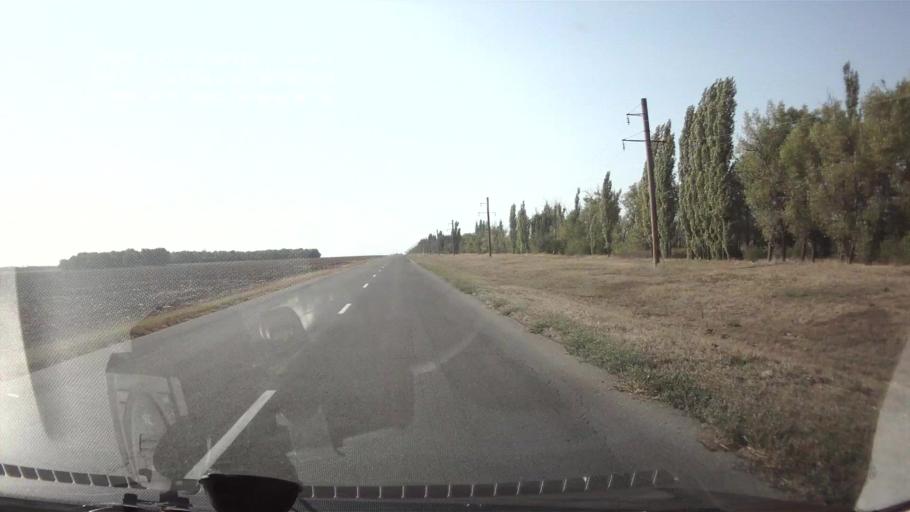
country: RU
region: Rostov
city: Tselina
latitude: 46.5321
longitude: 40.8998
